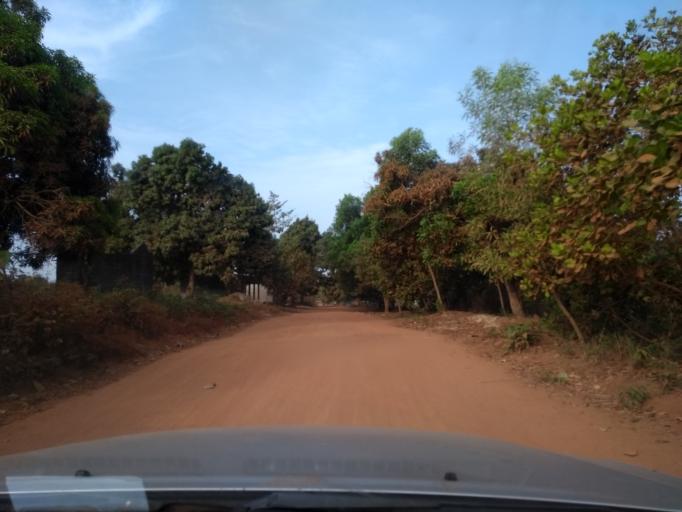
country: GN
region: Kindia
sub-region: Prefecture de Dubreka
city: Dubreka
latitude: 9.7884
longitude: -13.5342
